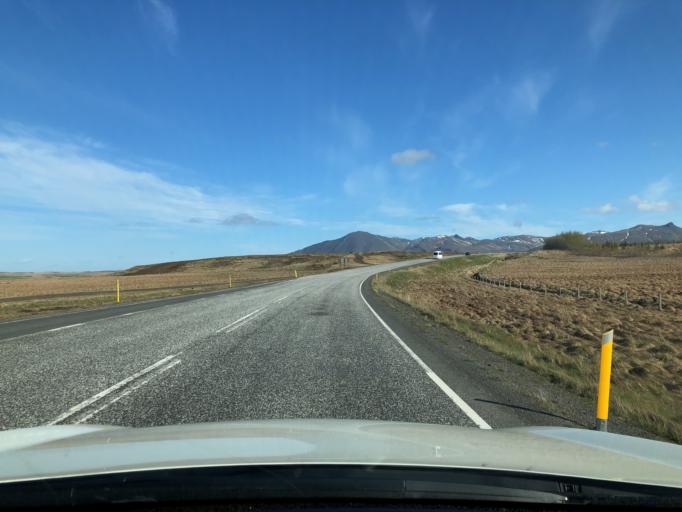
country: IS
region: West
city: Borgarnes
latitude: 64.3778
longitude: -21.8511
